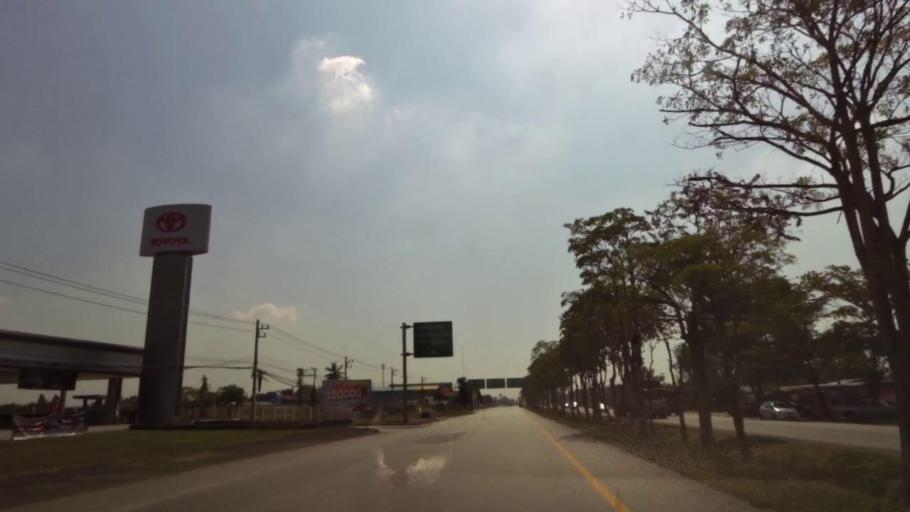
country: TH
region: Phichit
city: Bueng Na Rang
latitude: 16.1297
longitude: 100.1256
